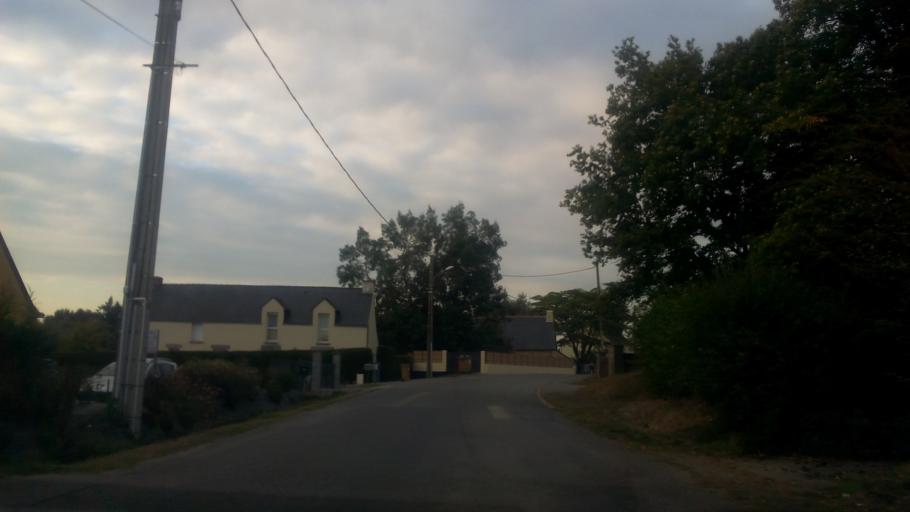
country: FR
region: Brittany
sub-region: Departement du Morbihan
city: Peillac
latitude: 47.7103
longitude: -2.2151
